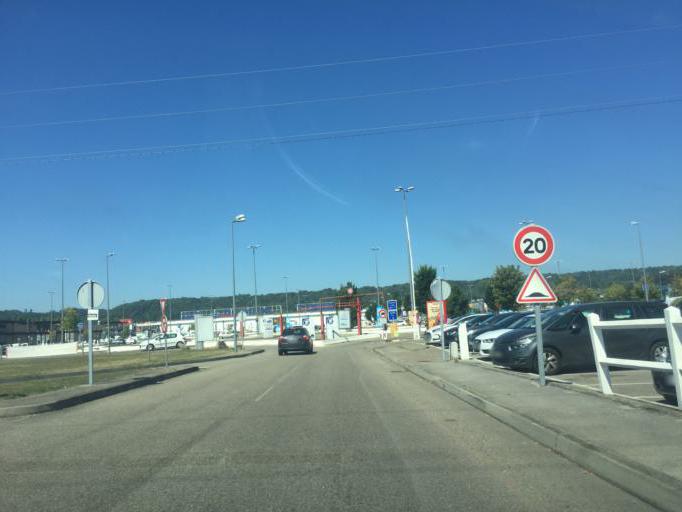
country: FR
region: Rhone-Alpes
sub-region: Departement de l'Ain
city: Beynost
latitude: 45.8230
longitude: 4.9984
